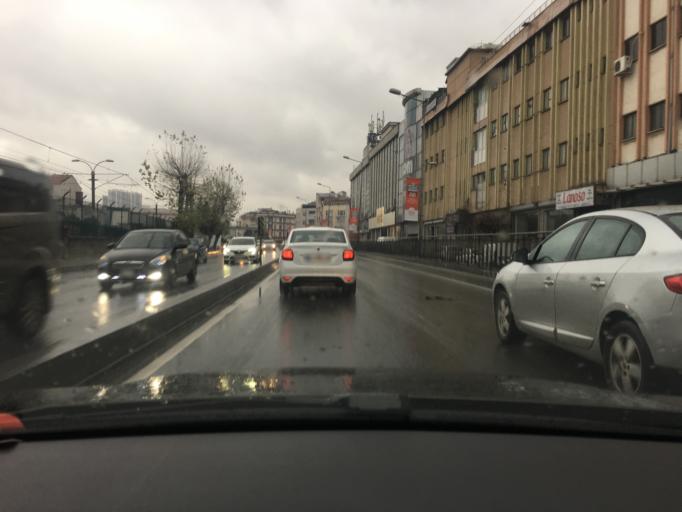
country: TR
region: Istanbul
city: merter keresteciler
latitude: 41.0289
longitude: 28.8990
